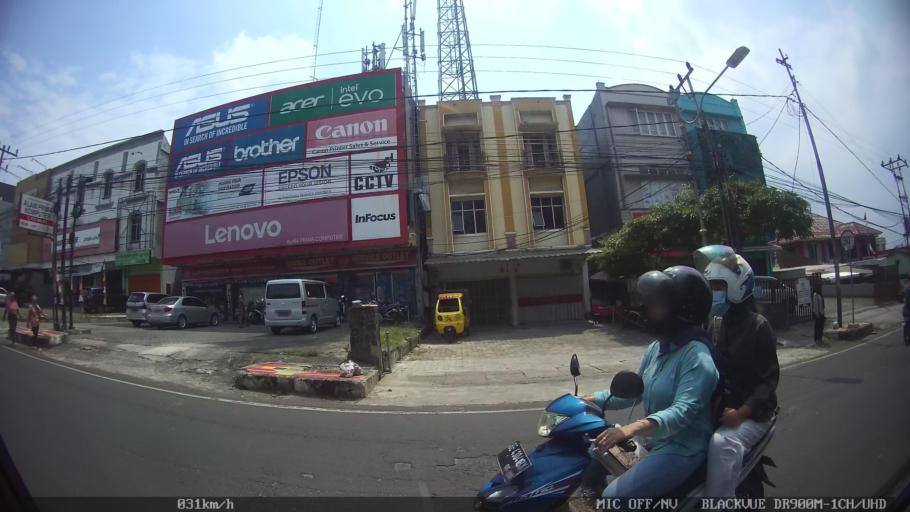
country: ID
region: Lampung
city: Bandarlampung
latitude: -5.4351
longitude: 105.2647
